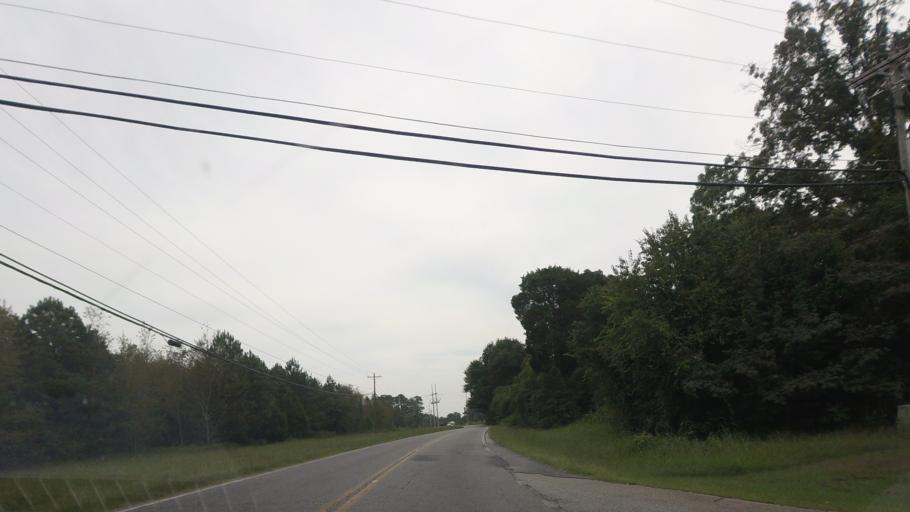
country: US
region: Georgia
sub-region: Houston County
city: Robins Air Force Base
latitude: 32.5918
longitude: -83.6067
